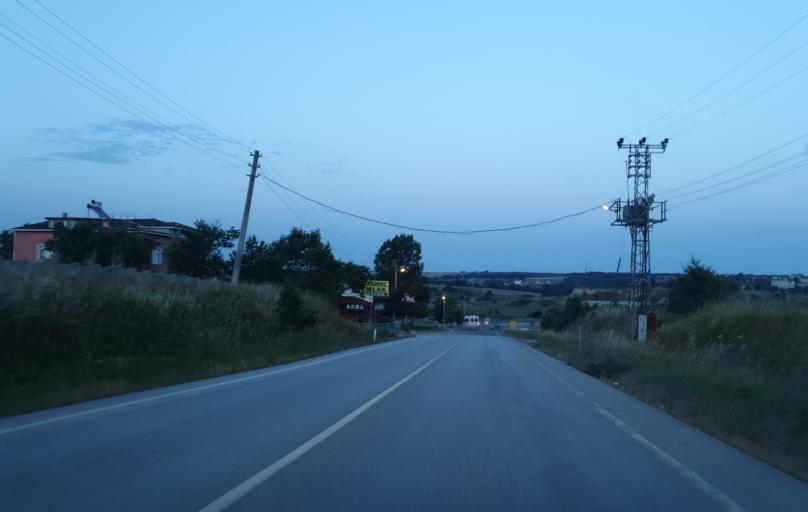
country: TR
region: Tekirdag
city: Saray
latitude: 41.3708
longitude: 27.9380
